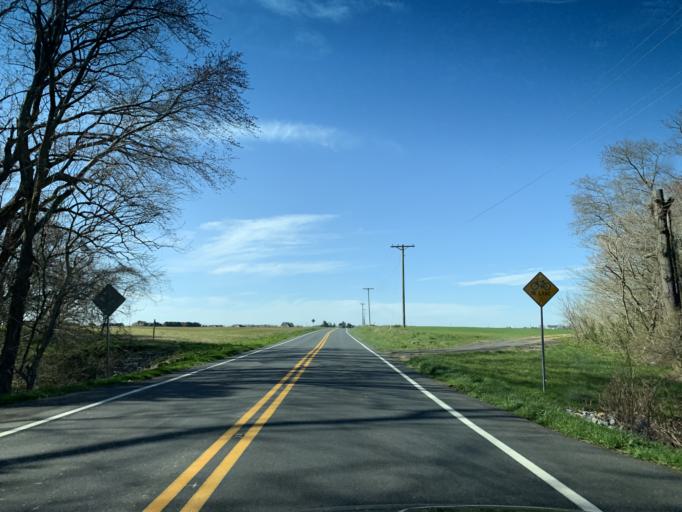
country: US
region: Delaware
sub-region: Kent County
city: Riverview
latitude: 38.9923
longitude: -75.5146
